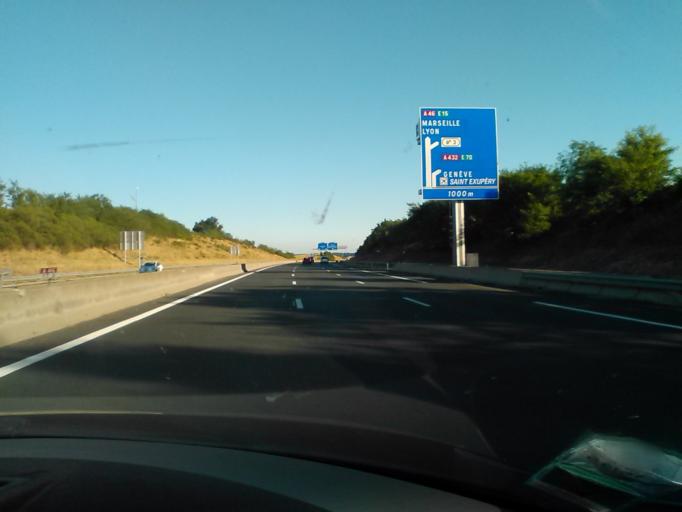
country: FR
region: Rhone-Alpes
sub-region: Departement de l'Ain
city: Mionnay
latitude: 45.8774
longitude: 4.9015
